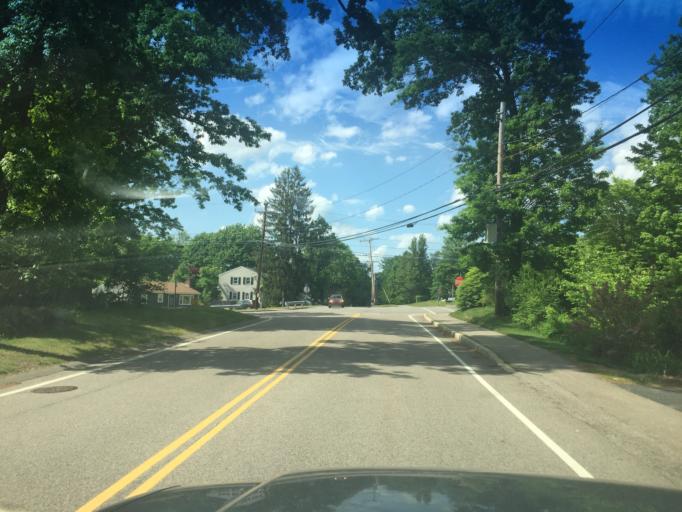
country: US
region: Massachusetts
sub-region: Norfolk County
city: Medway
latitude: 42.1565
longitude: -71.4202
